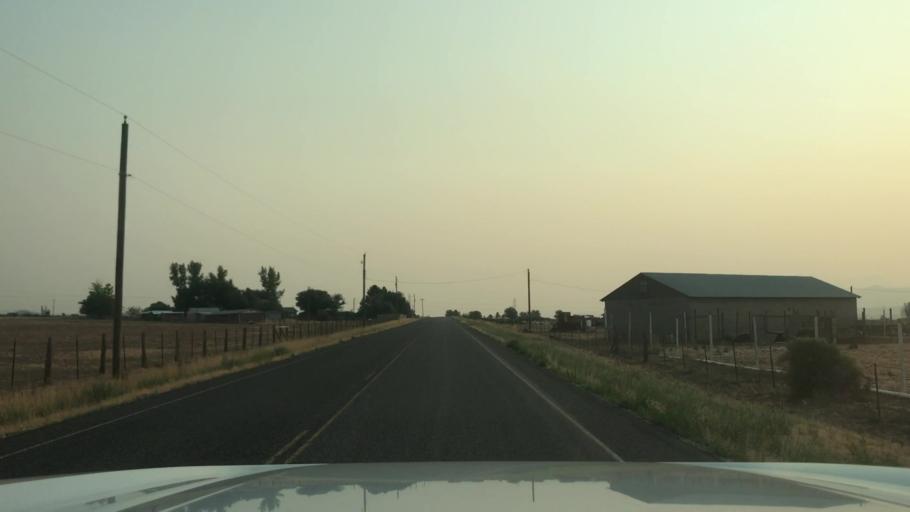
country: US
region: Utah
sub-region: Sevier County
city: Aurora
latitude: 38.8877
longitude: -111.9565
